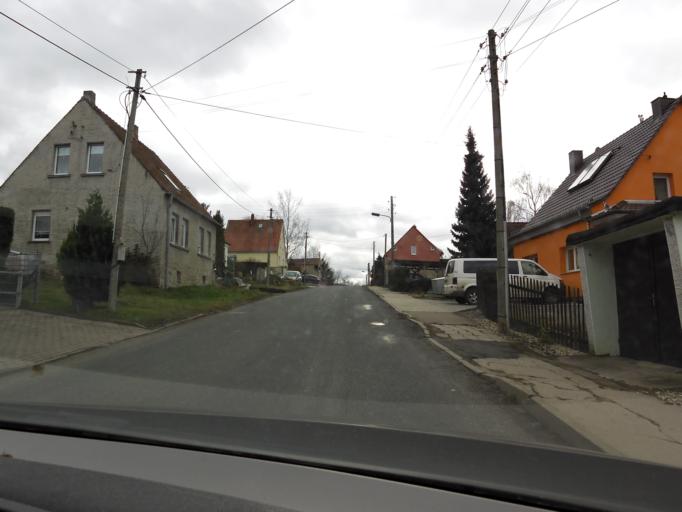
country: DE
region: Thuringia
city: Niederrossla
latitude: 51.0040
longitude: 11.4910
